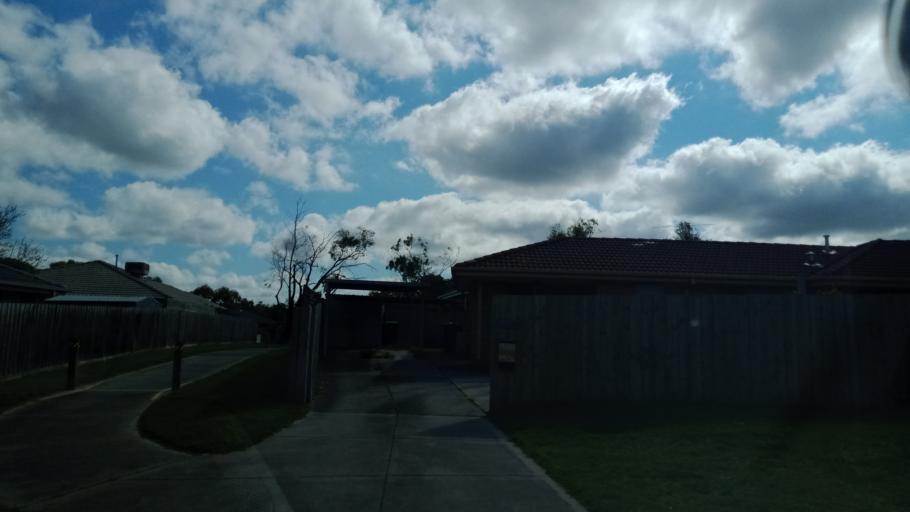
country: AU
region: Victoria
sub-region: Frankston
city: Carrum Downs
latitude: -38.0916
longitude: 145.1848
